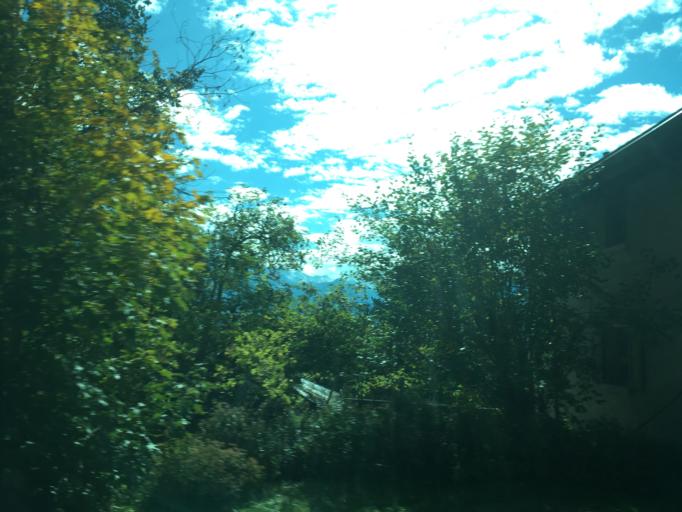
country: CH
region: Valais
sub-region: Sierre District
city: Chermignon-d'en Haut
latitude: 46.2975
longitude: 7.4833
